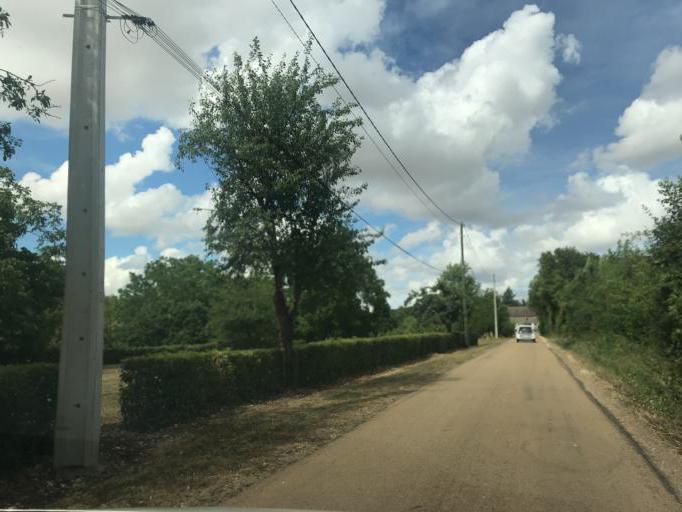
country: FR
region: Bourgogne
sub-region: Departement de l'Yonne
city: Fontenailles
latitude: 47.5651
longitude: 3.3414
